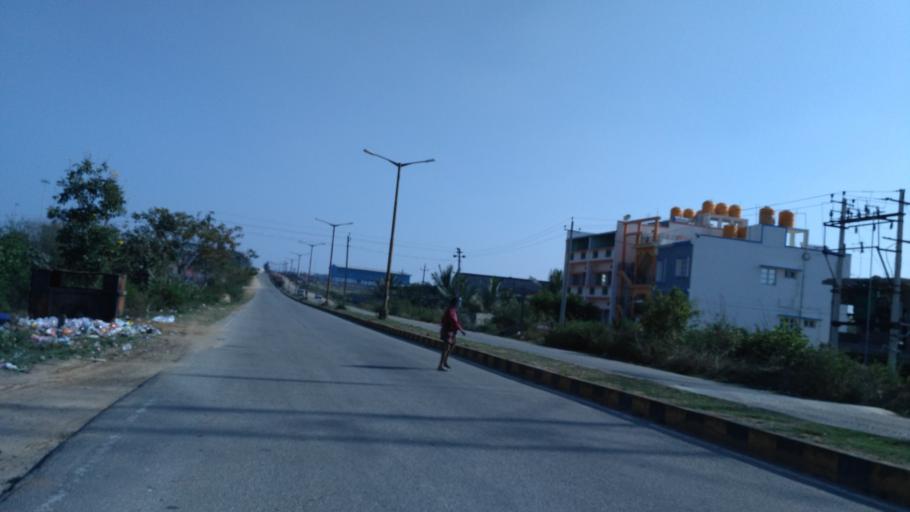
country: IN
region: Karnataka
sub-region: Hassan
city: Hassan
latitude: 12.9887
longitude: 76.1146
